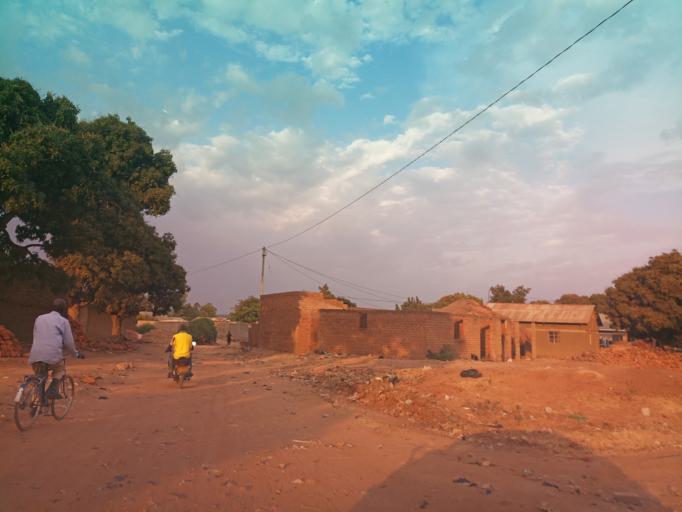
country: UG
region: Northern Region
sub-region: Arua District
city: Arua
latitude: 3.0332
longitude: 30.9153
